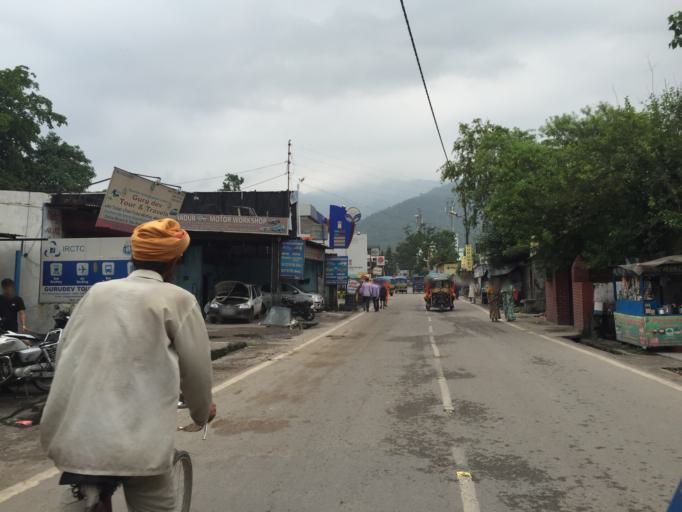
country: IN
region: Uttarakhand
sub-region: Dehradun
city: Rishikesh
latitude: 30.1111
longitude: 78.3029
